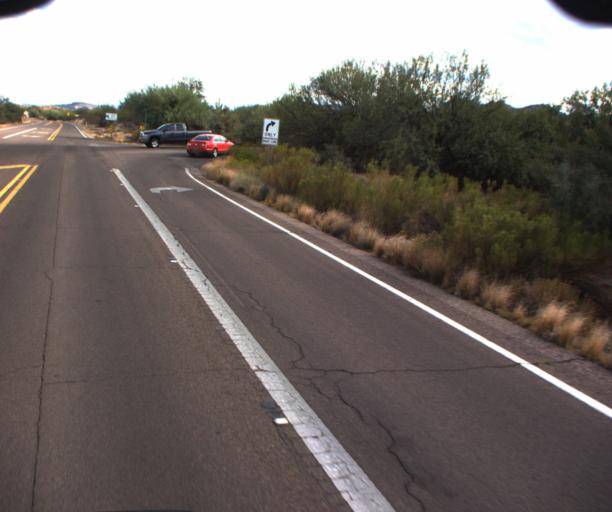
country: US
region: Arizona
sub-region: Pinal County
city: Apache Junction
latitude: 33.4641
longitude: -111.4825
